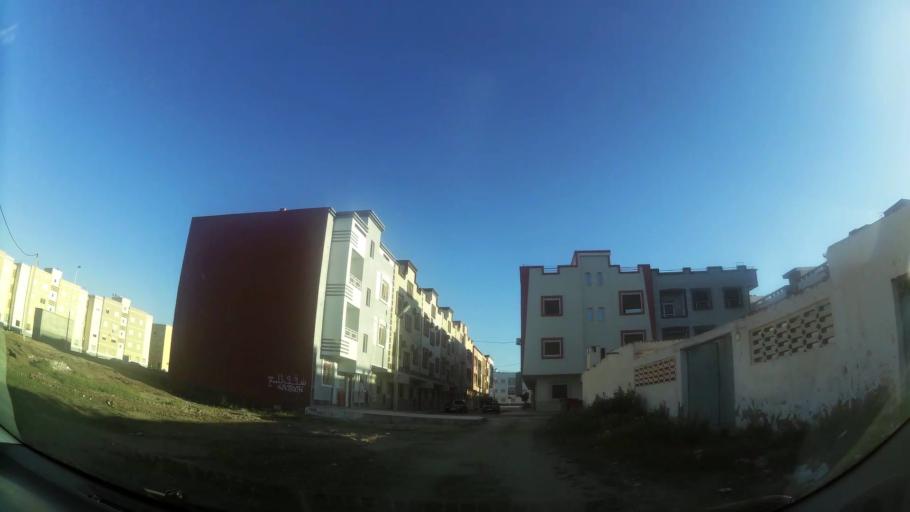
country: MA
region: Oriental
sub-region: Berkane-Taourirt
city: Madagh
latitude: 35.0821
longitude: -2.2377
